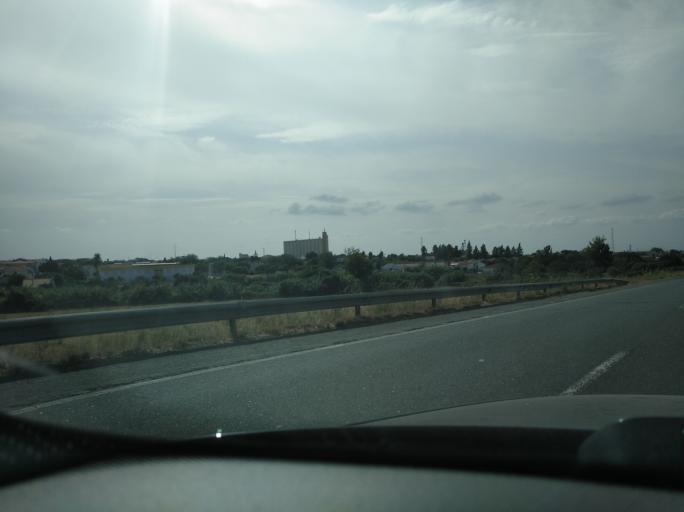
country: PT
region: Beja
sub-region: Beja
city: Ferreira do Alentejo
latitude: 38.0644
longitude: -8.1115
